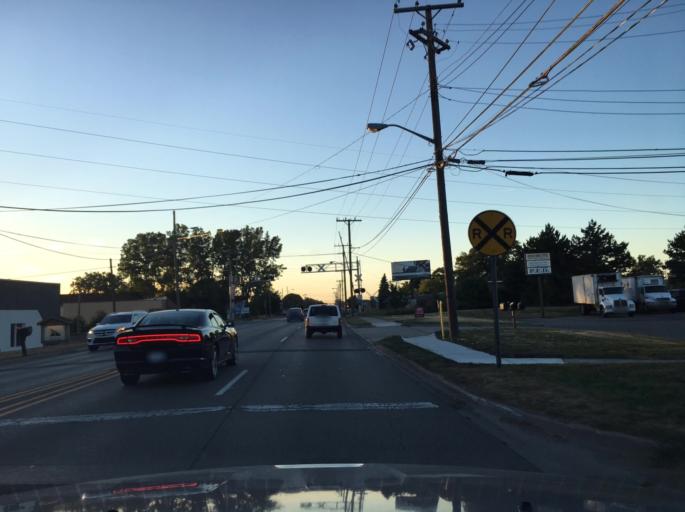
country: US
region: Michigan
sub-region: Macomb County
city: Fraser
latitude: 42.5272
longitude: -82.9460
